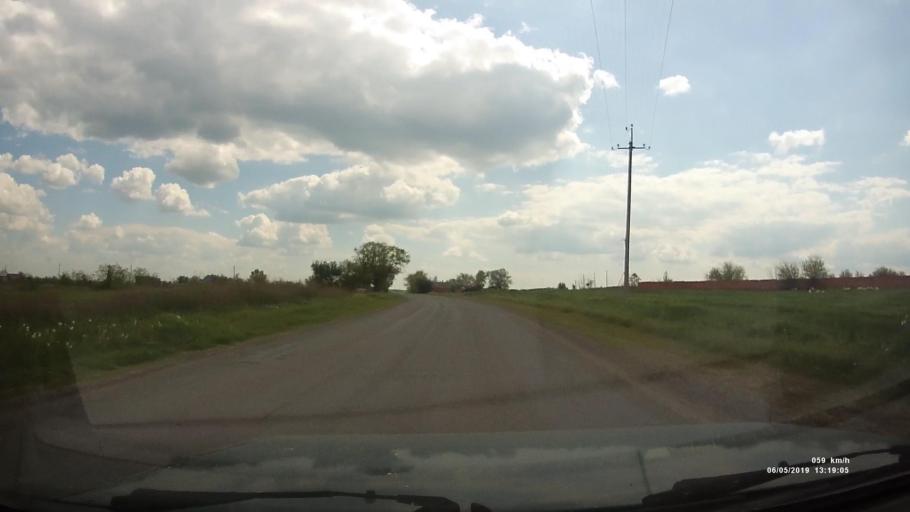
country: RU
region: Rostov
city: Ust'-Donetskiy
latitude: 47.7284
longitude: 40.9141
